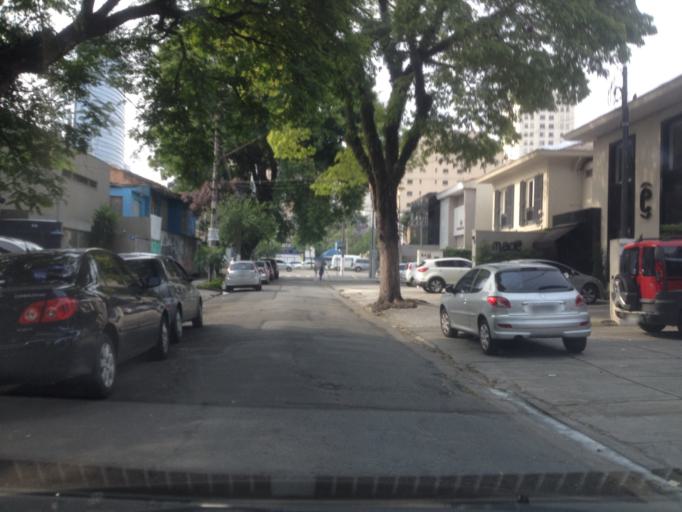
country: BR
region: Sao Paulo
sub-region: Sao Paulo
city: Sao Paulo
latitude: -23.5903
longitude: -46.6775
